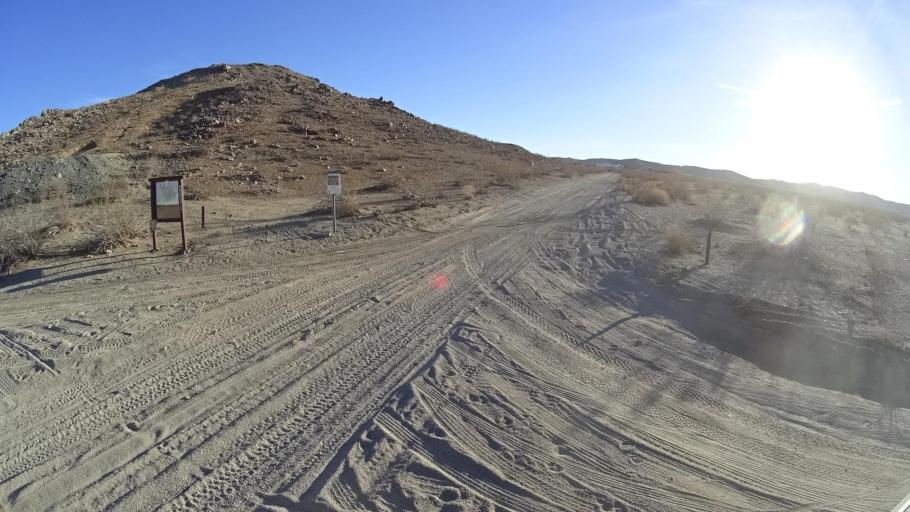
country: US
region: California
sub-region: Kern County
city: Ridgecrest
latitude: 35.5788
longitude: -117.6615
